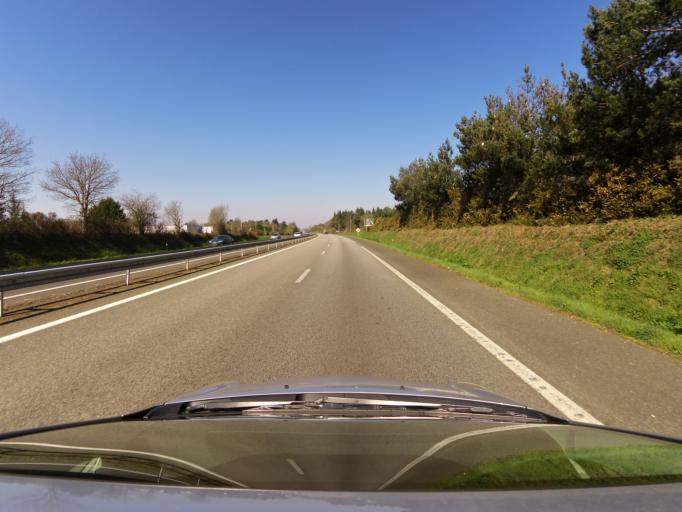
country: FR
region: Brittany
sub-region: Departement du Morbihan
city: Guillac
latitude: 47.9406
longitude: -2.4988
